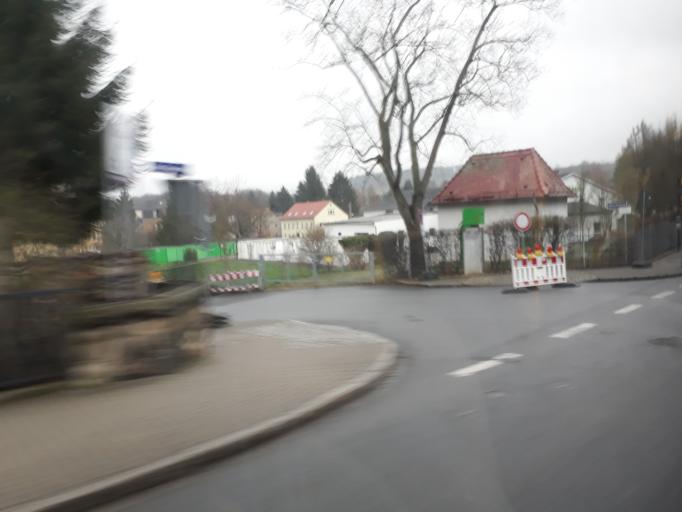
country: DE
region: Saxony
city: Kreischa
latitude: 50.9888
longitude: 13.8028
